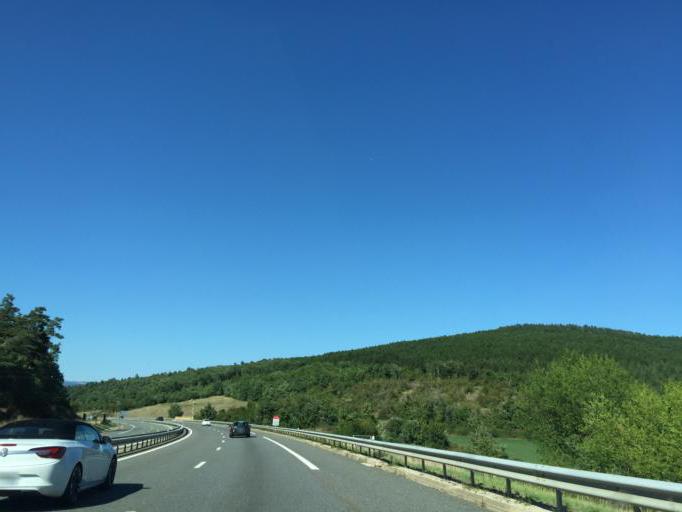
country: FR
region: Midi-Pyrenees
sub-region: Departement de l'Aveyron
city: Severac-le-Chateau
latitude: 44.3603
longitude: 3.1170
